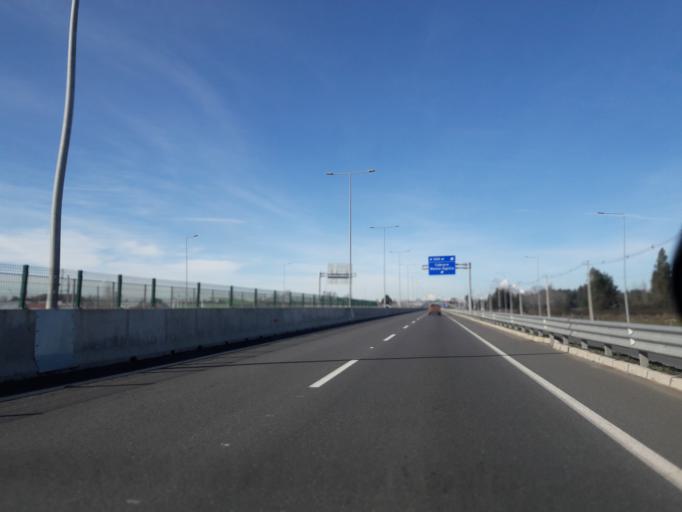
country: CL
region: Biobio
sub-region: Provincia de Biobio
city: Cabrero
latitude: -37.0351
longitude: -72.4151
